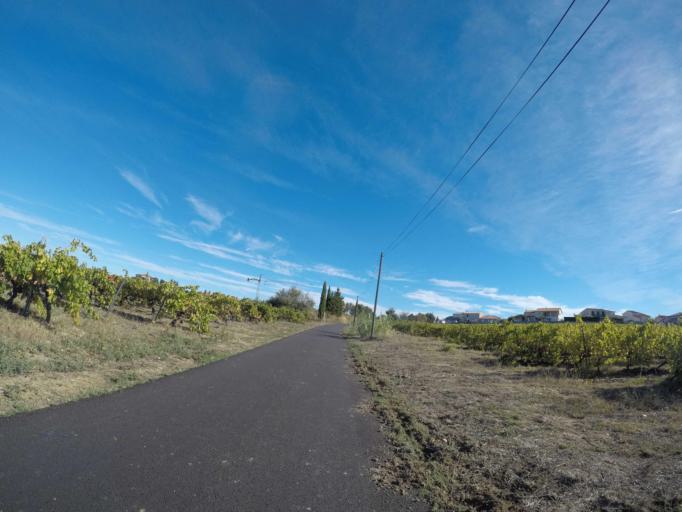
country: FR
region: Languedoc-Roussillon
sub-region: Departement des Pyrenees-Orientales
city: Villemolaque
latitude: 42.5760
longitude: 2.8064
